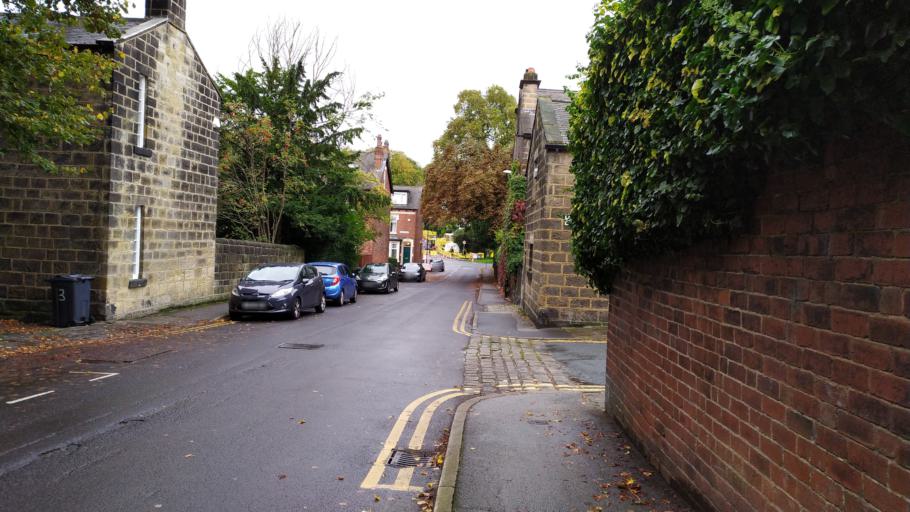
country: GB
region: England
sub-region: City and Borough of Leeds
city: Chapel Allerton
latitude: 53.8251
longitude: -1.5723
